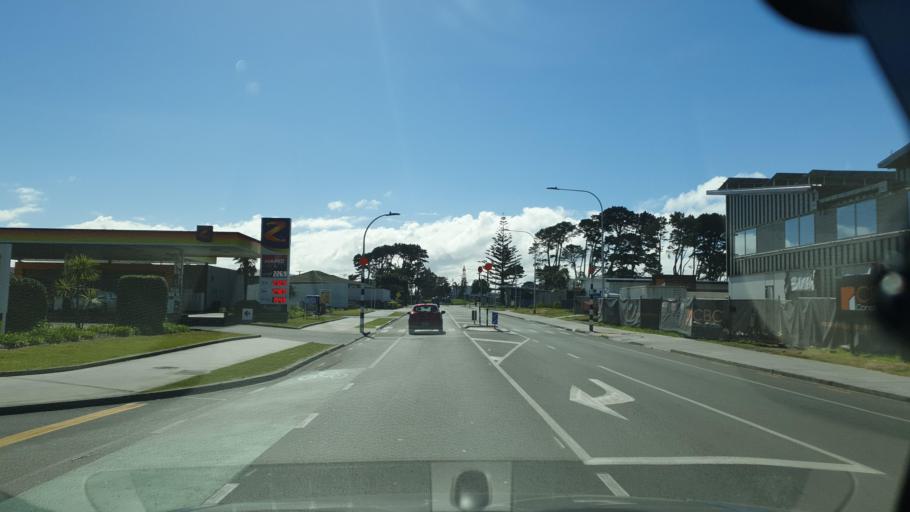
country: NZ
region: Bay of Plenty
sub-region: Tauranga City
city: Tauranga
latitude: -37.6996
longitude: 176.2847
